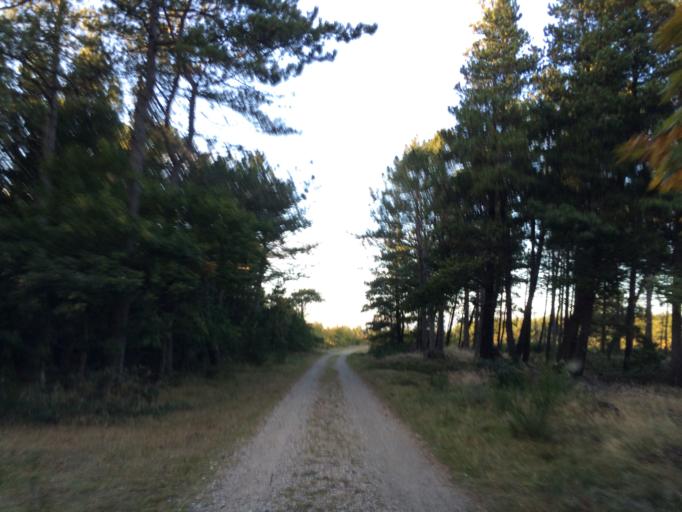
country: DK
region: Central Jutland
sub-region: Holstebro Kommune
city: Ulfborg
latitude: 56.3027
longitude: 8.1526
